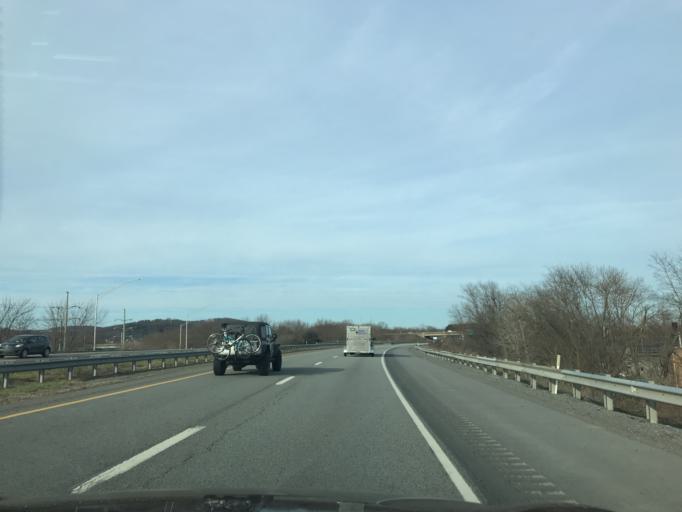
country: US
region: Pennsylvania
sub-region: Lycoming County
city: Duboistown
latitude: 41.2291
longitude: -77.0459
